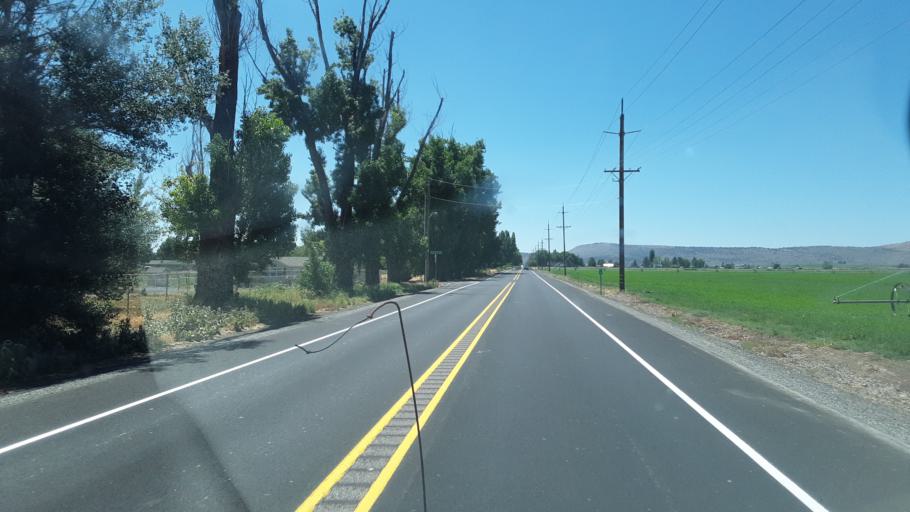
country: US
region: Oregon
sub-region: Klamath County
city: Altamont
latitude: 42.1387
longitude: -121.6983
